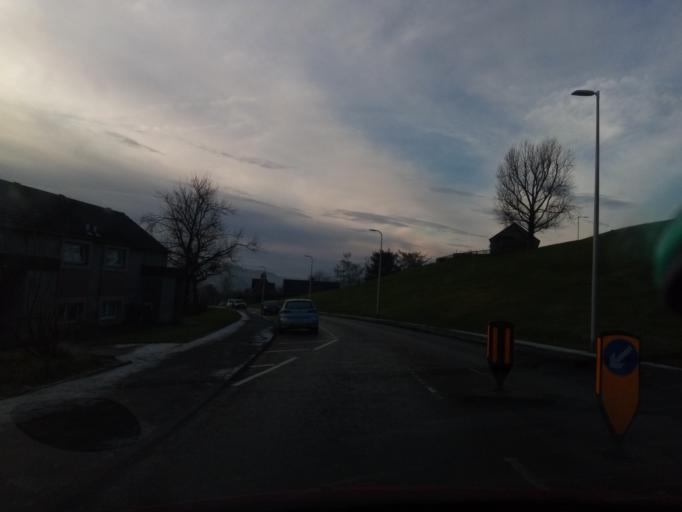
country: GB
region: Scotland
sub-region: The Scottish Borders
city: Hawick
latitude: 55.4345
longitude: -2.7734
